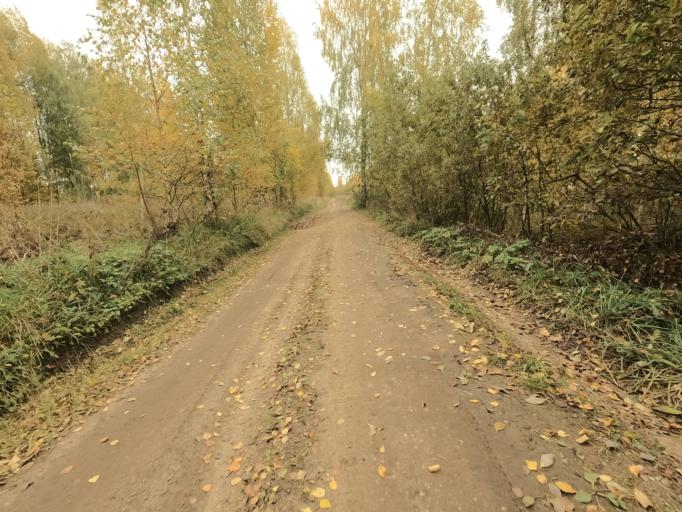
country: RU
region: Novgorod
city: Pankovka
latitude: 58.8663
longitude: 30.9239
